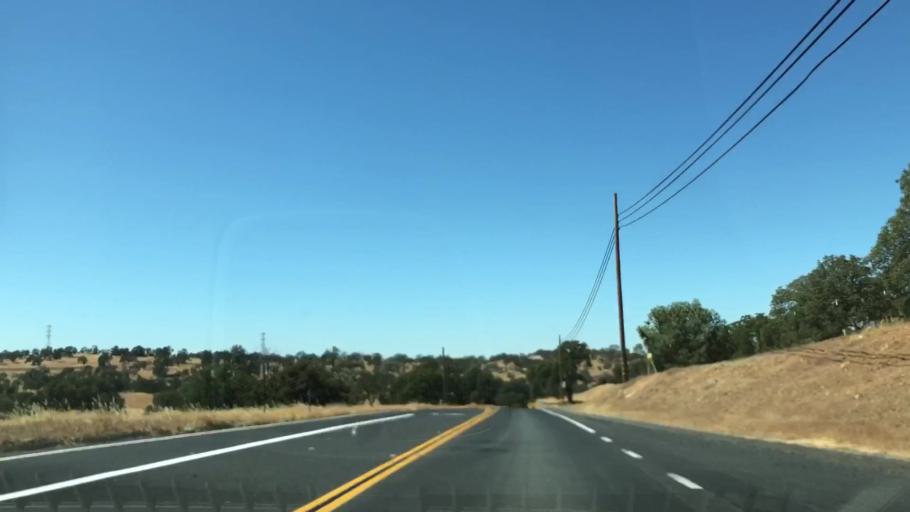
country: US
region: California
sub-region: Tuolumne County
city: Jamestown
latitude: 37.8880
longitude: -120.5376
